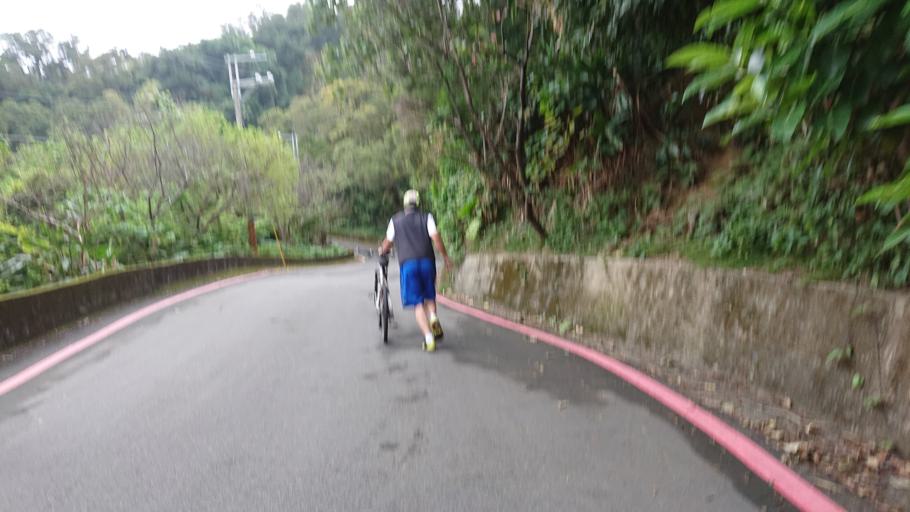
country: TW
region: Taiwan
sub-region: Taoyuan
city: Taoyuan
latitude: 24.9331
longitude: 121.3669
